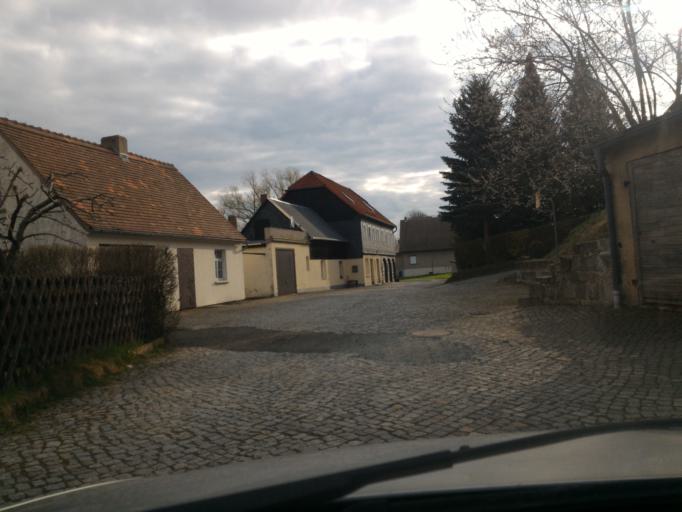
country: DE
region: Saxony
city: Eibau
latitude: 50.9756
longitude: 14.6894
